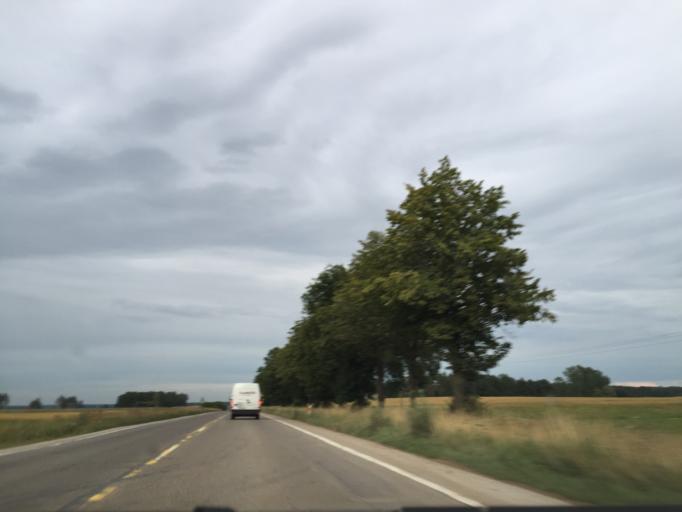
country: PL
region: Podlasie
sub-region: Powiat wysokomazowiecki
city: Sokoly
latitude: 53.1149
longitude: 22.6183
